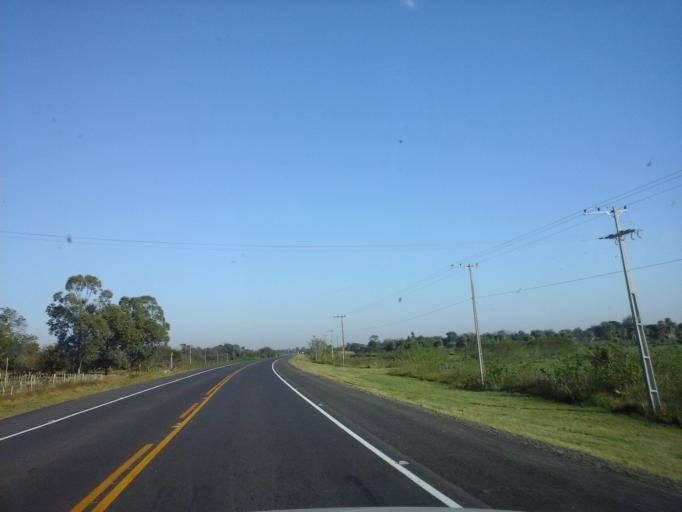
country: PY
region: Neembucu
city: Pilar
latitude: -26.8672
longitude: -58.1239
